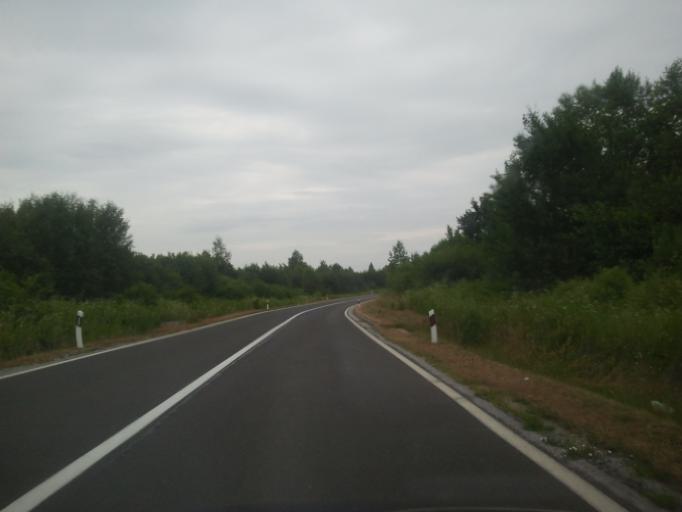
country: HR
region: Sisacko-Moslavacka
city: Gvozd
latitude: 45.3227
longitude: 15.9451
